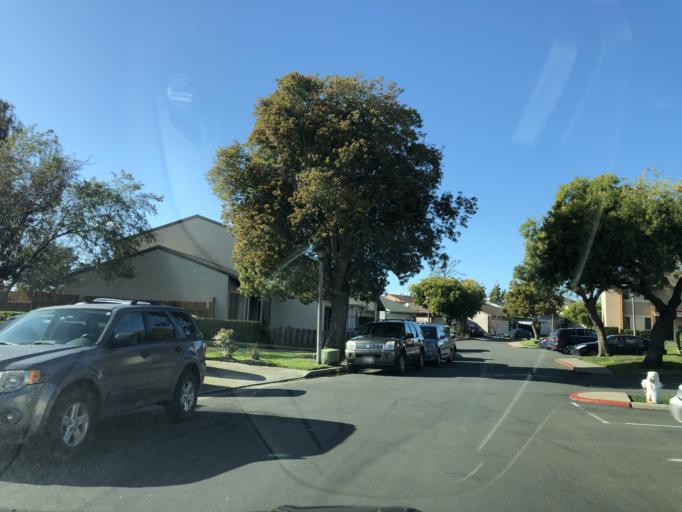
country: US
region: California
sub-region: Contra Costa County
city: Tara Hills
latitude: 37.9817
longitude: -122.3098
